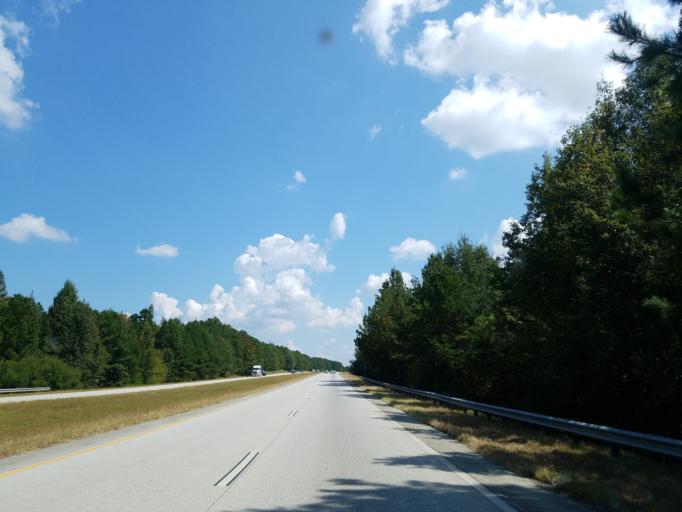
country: US
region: Georgia
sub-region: Barrow County
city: Statham
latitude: 33.9539
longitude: -83.5991
